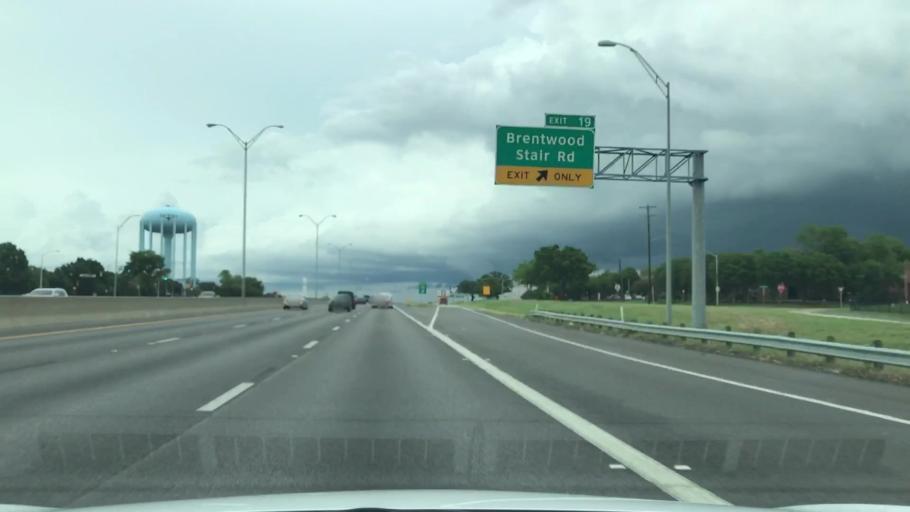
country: US
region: Texas
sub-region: Tarrant County
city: Haltom City
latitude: 32.7592
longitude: -97.2582
